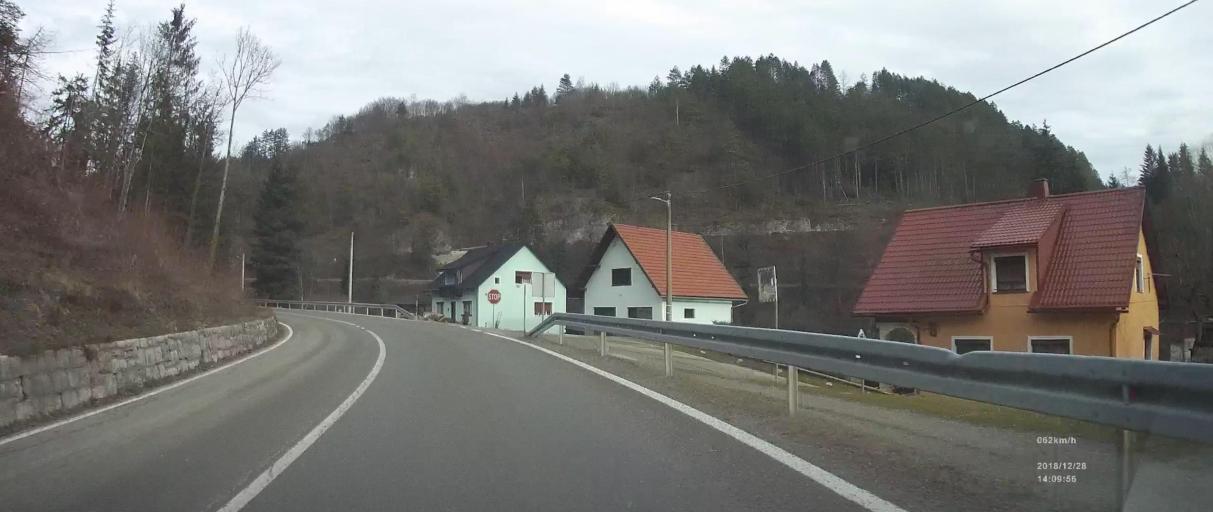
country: SI
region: Kostel
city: Kostel
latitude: 45.4495
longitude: 14.9772
